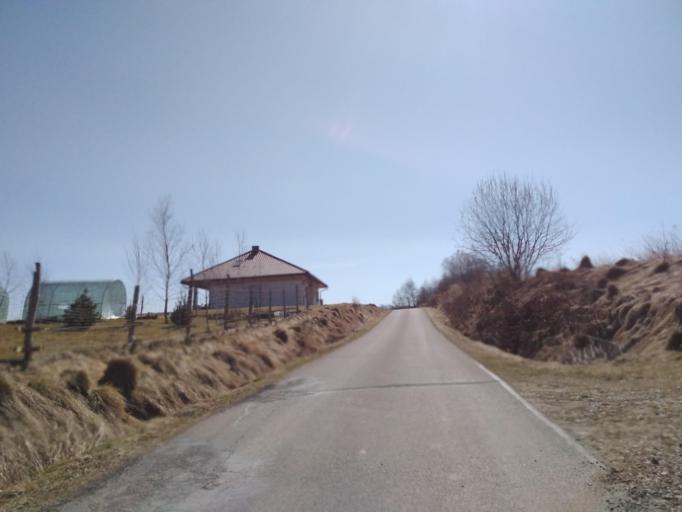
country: PL
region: Subcarpathian Voivodeship
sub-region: Powiat brzozowski
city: Orzechowka
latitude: 49.7142
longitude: 21.9667
